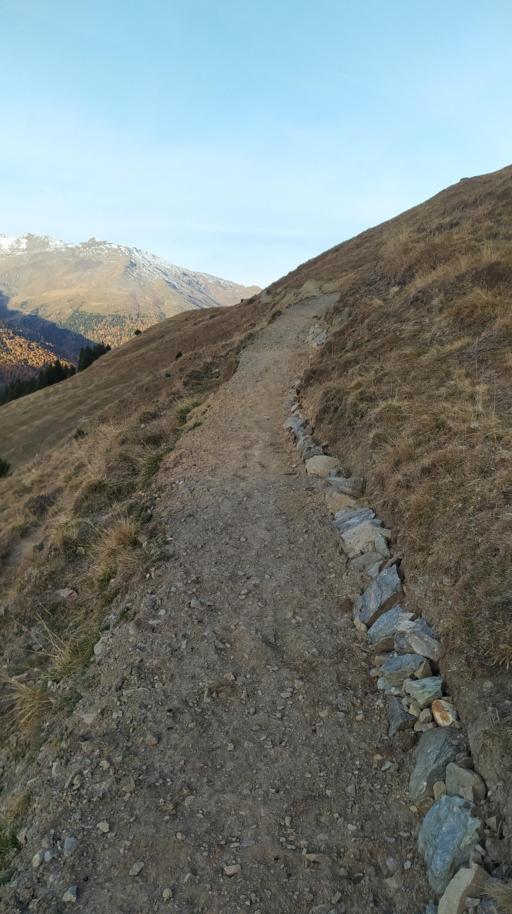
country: IT
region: Lombardy
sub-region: Provincia di Sondrio
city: Sant'Antonio
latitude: 46.4226
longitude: 10.5029
